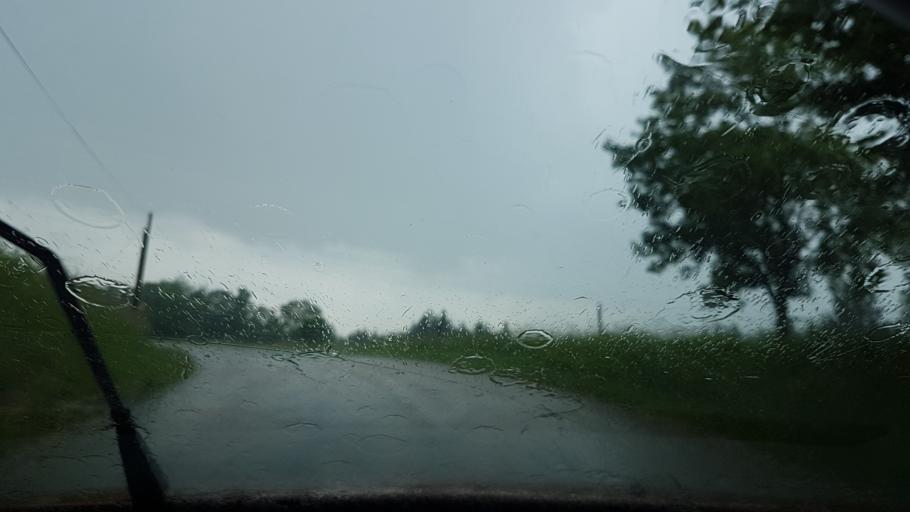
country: FR
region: Franche-Comte
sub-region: Departement du Jura
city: Clairvaux-les-Lacs
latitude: 46.5778
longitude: 5.7050
